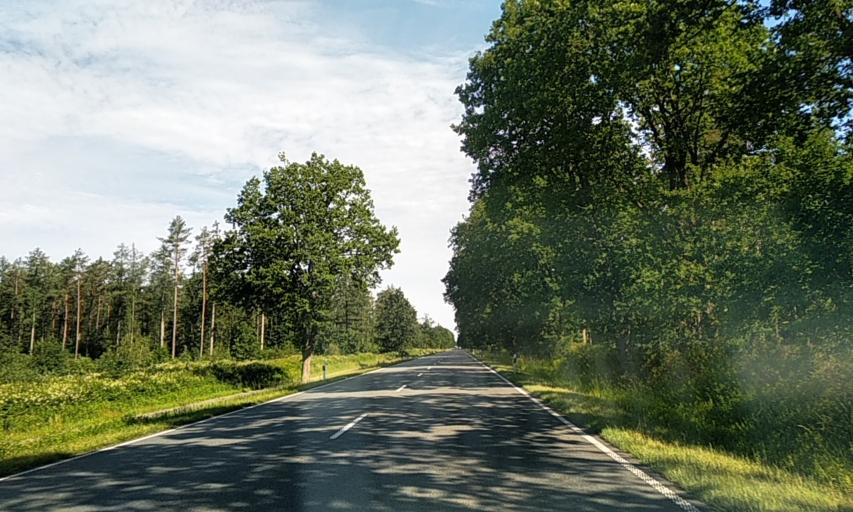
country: DE
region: Schleswig-Holstein
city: Kropp
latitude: 54.3815
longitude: 9.5443
